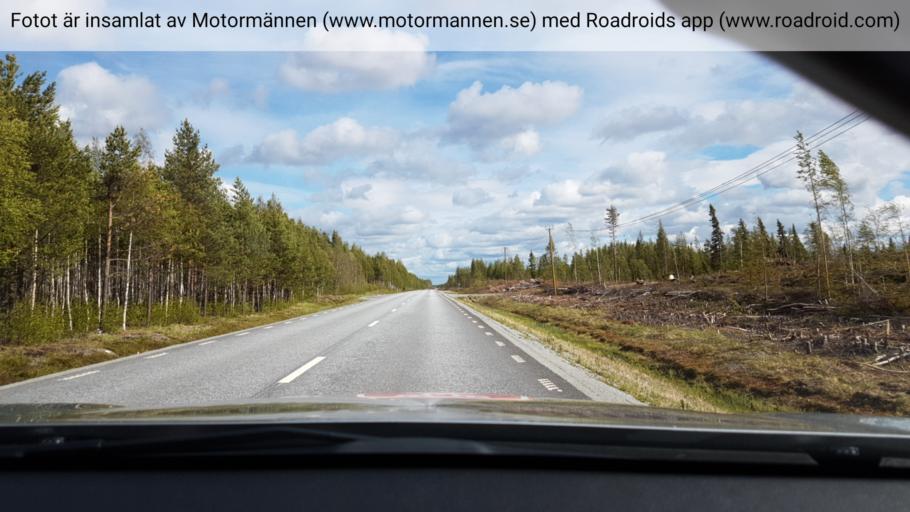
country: SE
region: Vaesternorrland
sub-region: OErnskoeldsviks Kommun
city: Bredbyn
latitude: 64.1033
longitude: 18.1500
